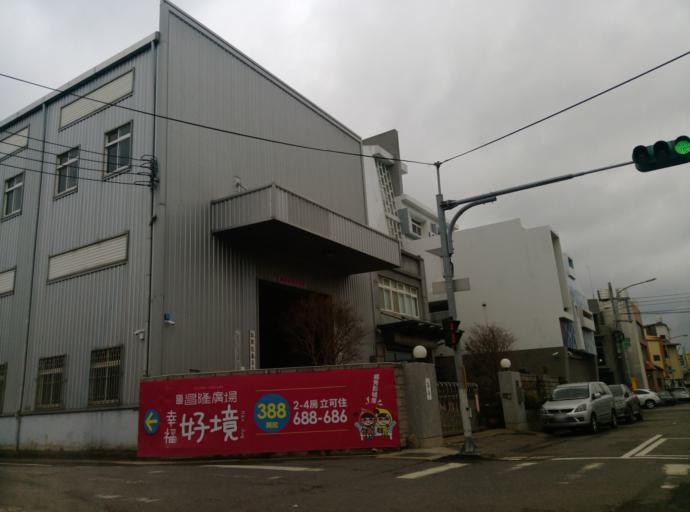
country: TW
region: Taiwan
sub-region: Hsinchu
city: Hsinchu
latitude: 24.6889
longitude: 120.8931
